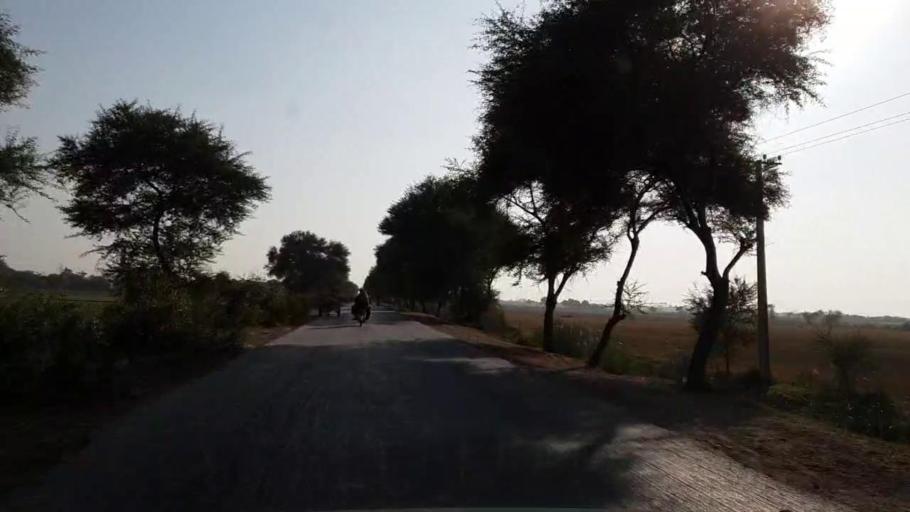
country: PK
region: Sindh
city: Bulri
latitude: 24.8769
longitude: 68.3404
